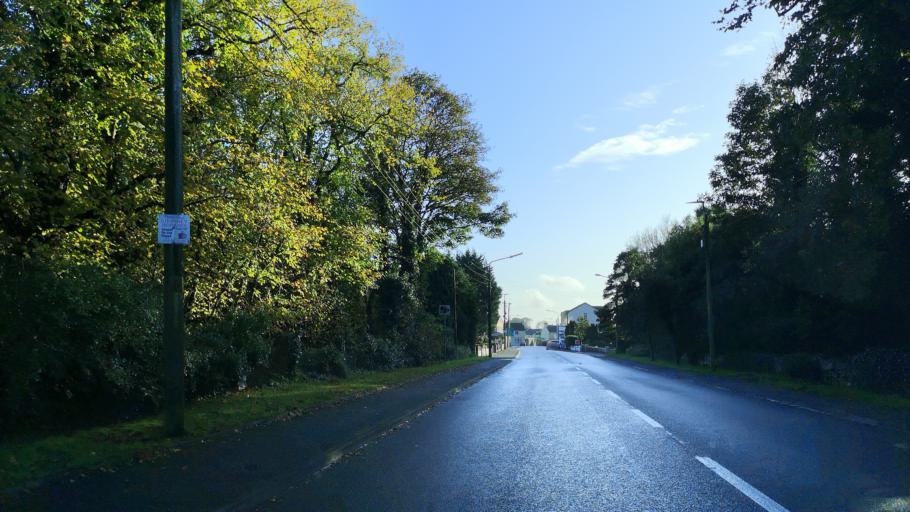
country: IE
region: Connaught
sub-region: Roscommon
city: Castlerea
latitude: 53.7715
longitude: -8.4938
